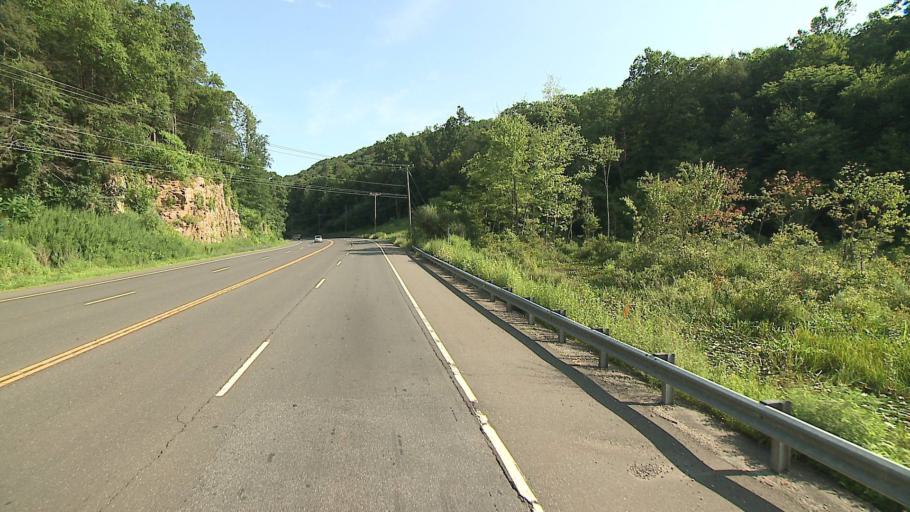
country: US
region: Connecticut
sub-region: Fairfield County
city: Danbury
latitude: 41.3519
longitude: -73.4694
